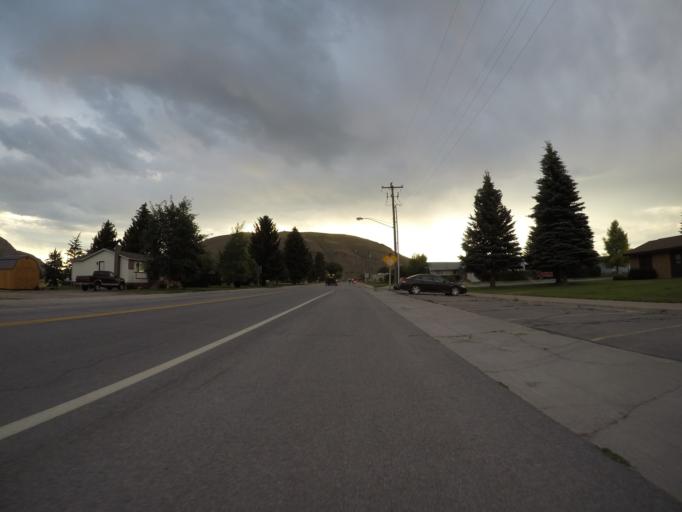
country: US
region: Idaho
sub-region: Bear Lake County
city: Montpelier
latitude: 42.0854
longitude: -110.9509
